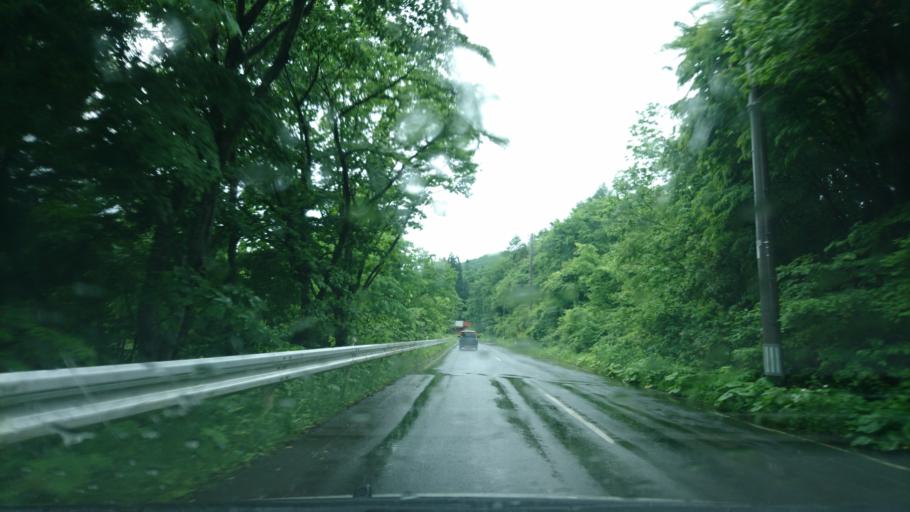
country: JP
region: Iwate
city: Ichinoseki
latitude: 39.0103
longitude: 140.8906
